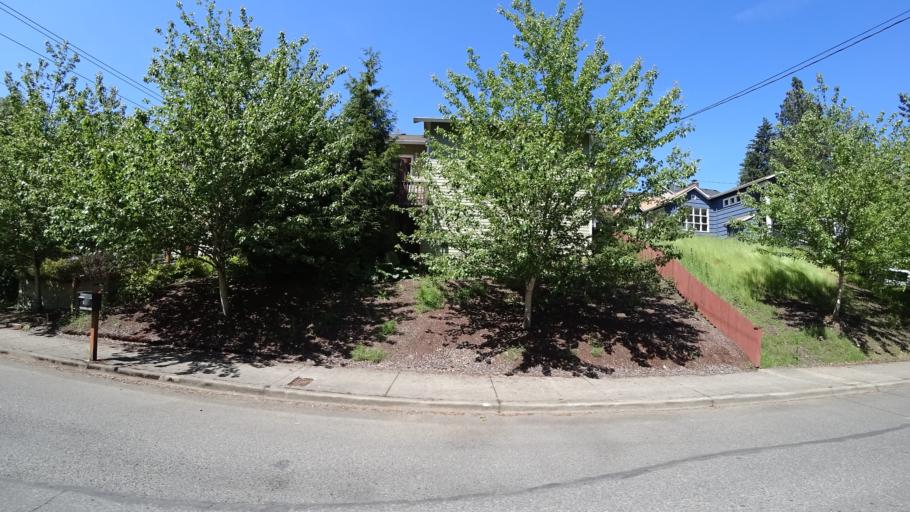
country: US
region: Oregon
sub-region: Washington County
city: Metzger
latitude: 45.4447
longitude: -122.7125
